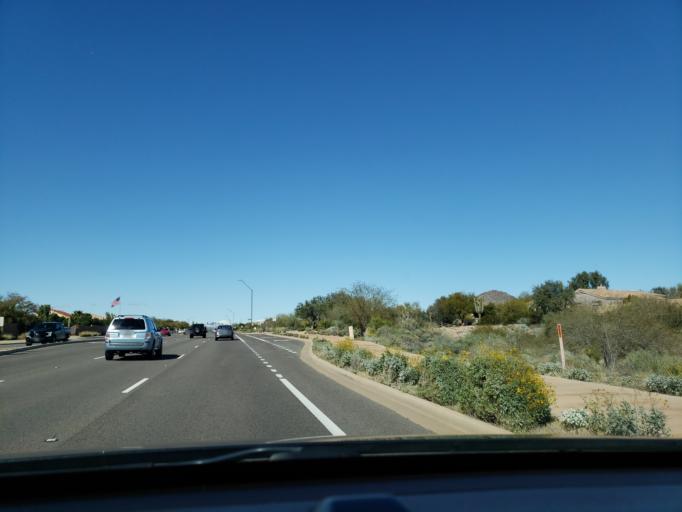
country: US
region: Arizona
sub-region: Maricopa County
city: Carefree
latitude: 33.6941
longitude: -111.8904
